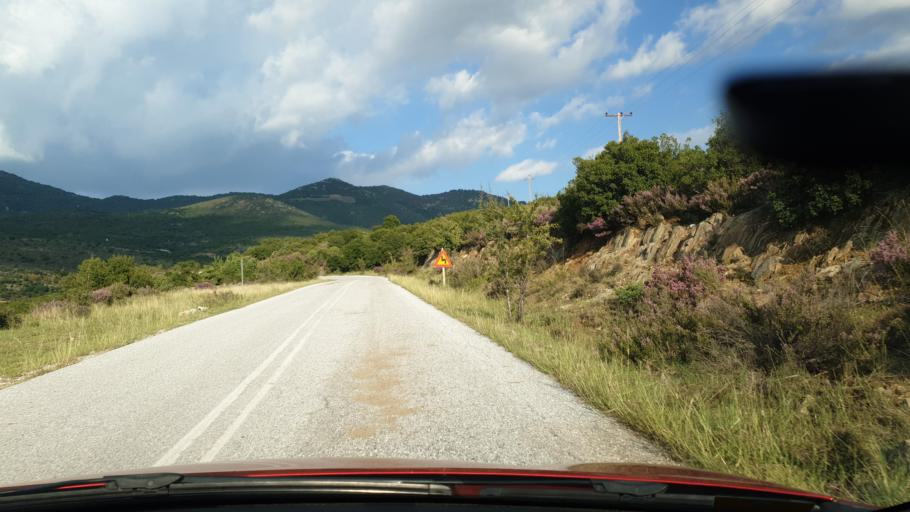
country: GR
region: Central Macedonia
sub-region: Nomos Thessalonikis
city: Peristera
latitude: 40.5160
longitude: 23.1750
